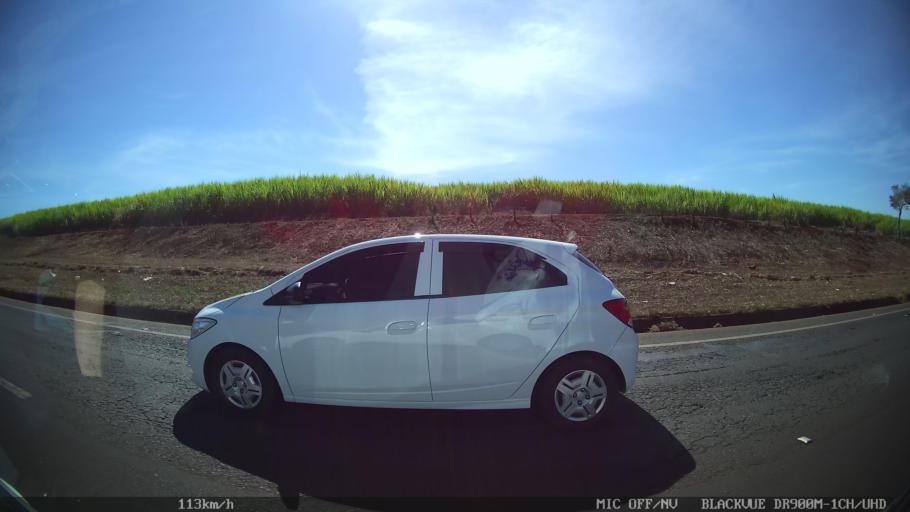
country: BR
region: Sao Paulo
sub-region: Ipua
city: Ipua
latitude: -20.4934
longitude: -48.0257
